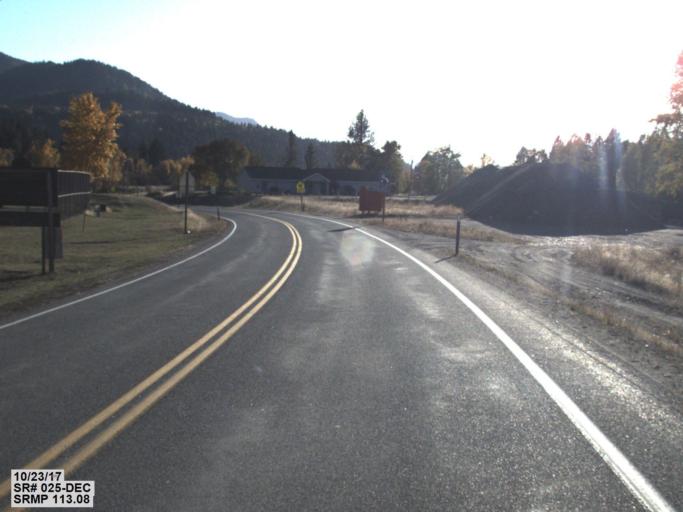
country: CA
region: British Columbia
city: Rossland
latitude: 48.9129
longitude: -117.7898
